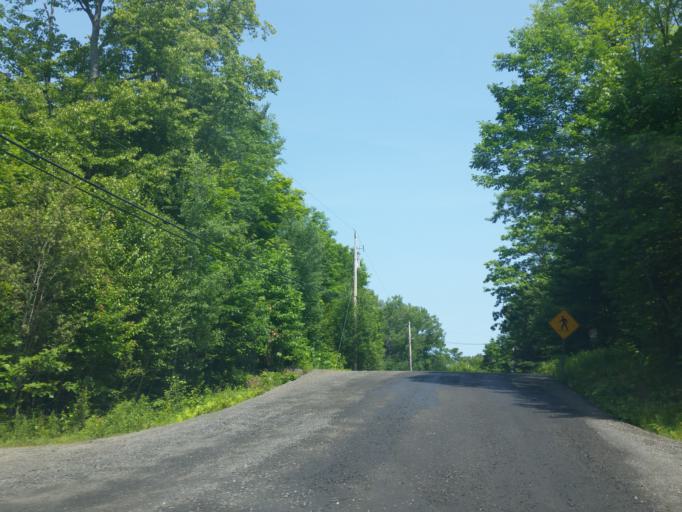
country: CA
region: Ontario
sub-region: Parry Sound District
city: Parry Sound
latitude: 45.4346
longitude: -80.0036
